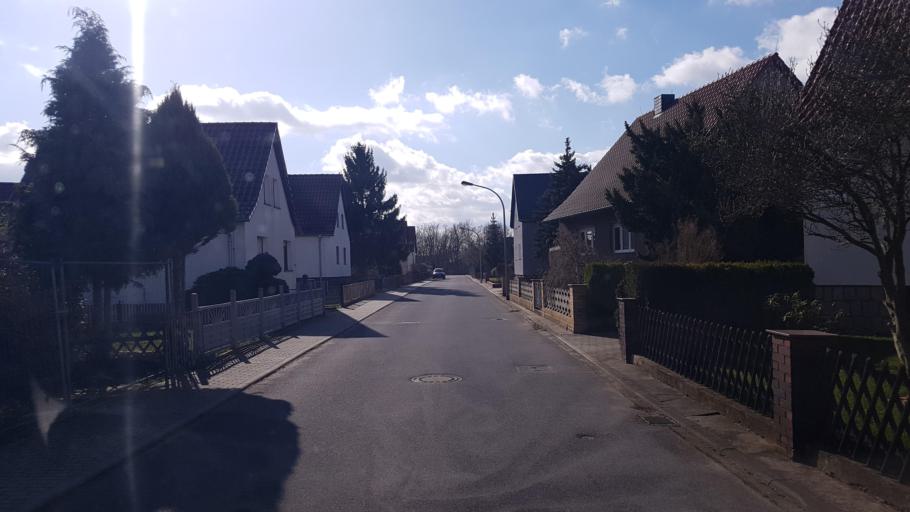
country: DE
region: Brandenburg
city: Herzberg
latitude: 51.6992
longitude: 13.2301
